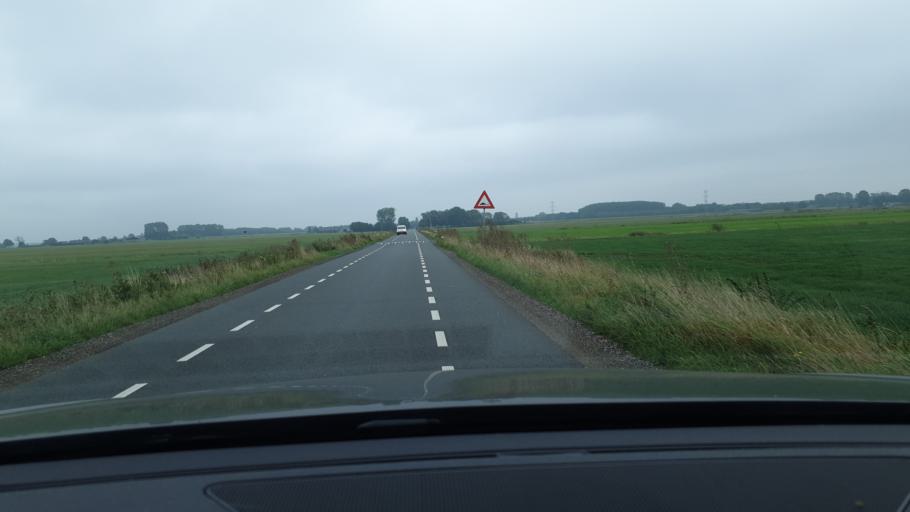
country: NL
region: North Brabant
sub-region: Gemeente Maasdonk
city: Geffen
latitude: 51.7716
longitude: 5.4703
